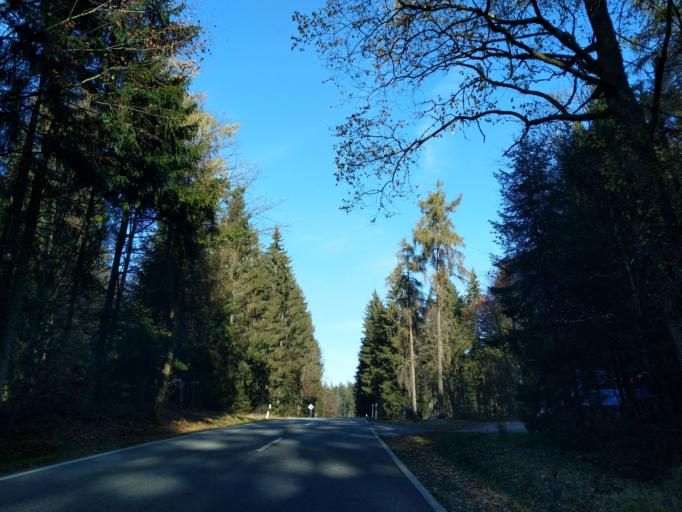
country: DE
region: Bavaria
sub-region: Lower Bavaria
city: Lalling
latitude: 48.8787
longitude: 13.1276
